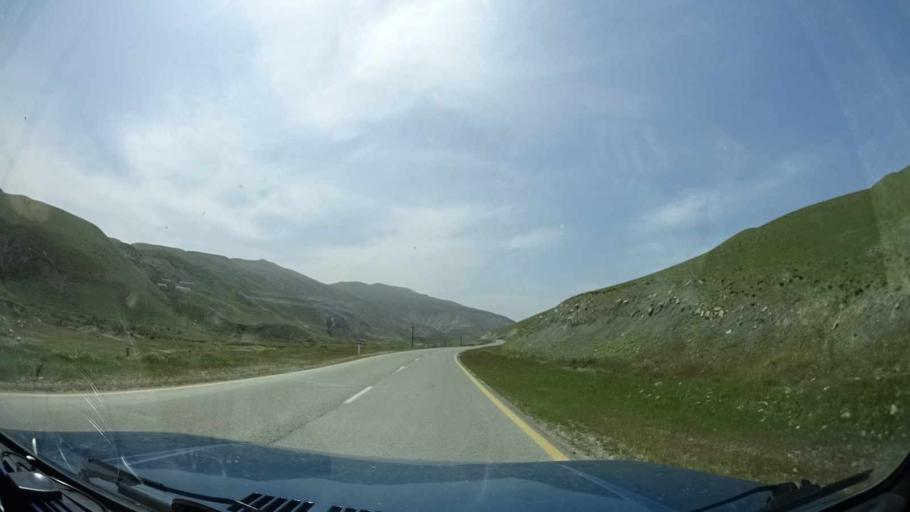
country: AZ
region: Xizi
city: Kilyazi
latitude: 40.8519
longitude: 49.3151
